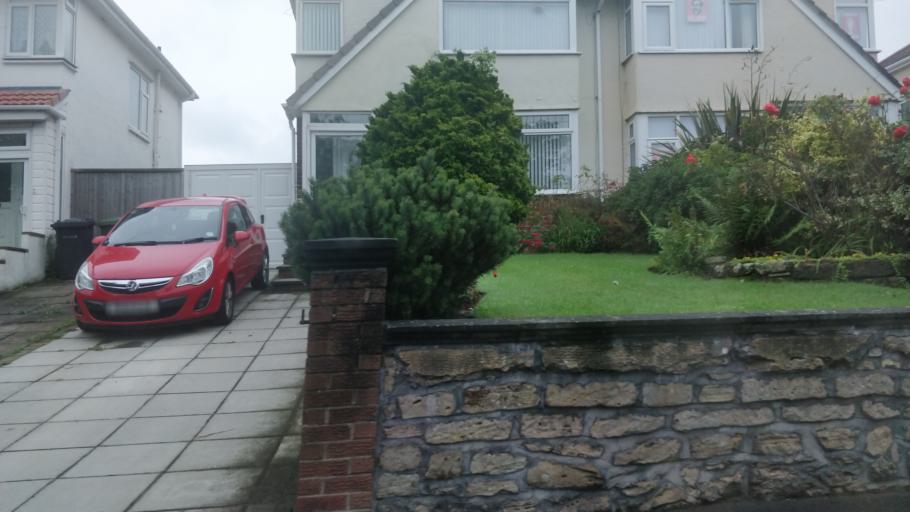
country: GB
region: England
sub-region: Sefton
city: Maghull
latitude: 53.5175
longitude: -2.9459
